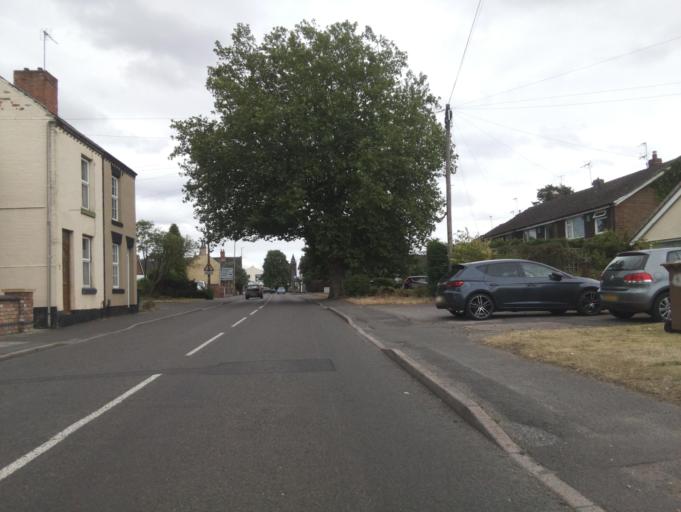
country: GB
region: England
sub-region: Derbyshire
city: Borrowash
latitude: 52.9072
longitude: -1.3837
